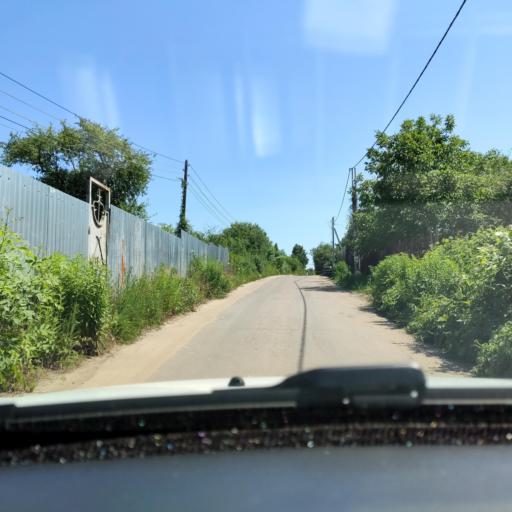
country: RU
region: Voronezj
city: Shilovo
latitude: 51.5913
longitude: 39.1485
